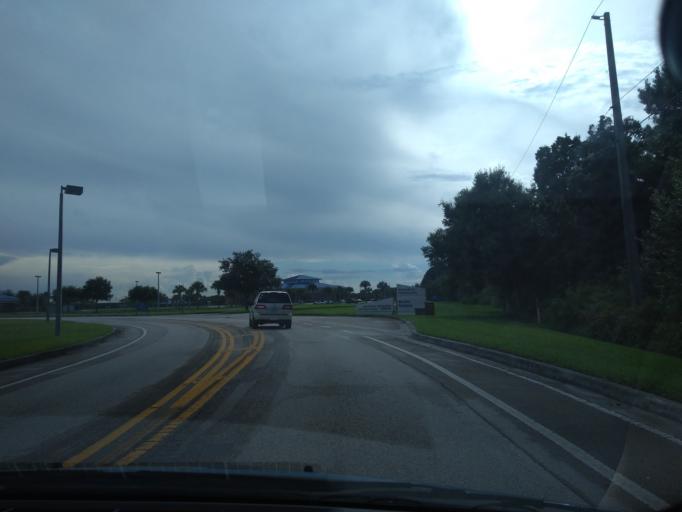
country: US
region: Florida
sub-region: Indian River County
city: West Vero Corridor
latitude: 27.6351
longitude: -80.4543
